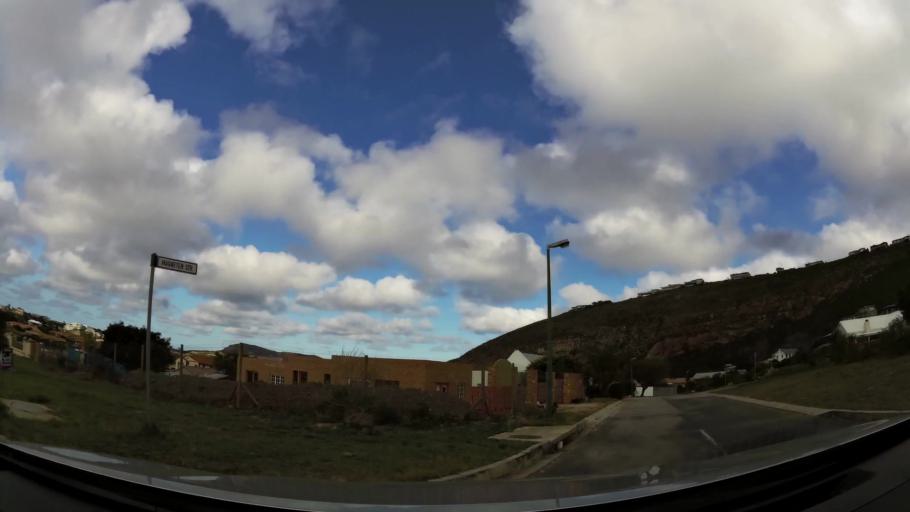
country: ZA
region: Western Cape
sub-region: Eden District Municipality
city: Plettenberg Bay
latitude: -34.0861
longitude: 23.3616
